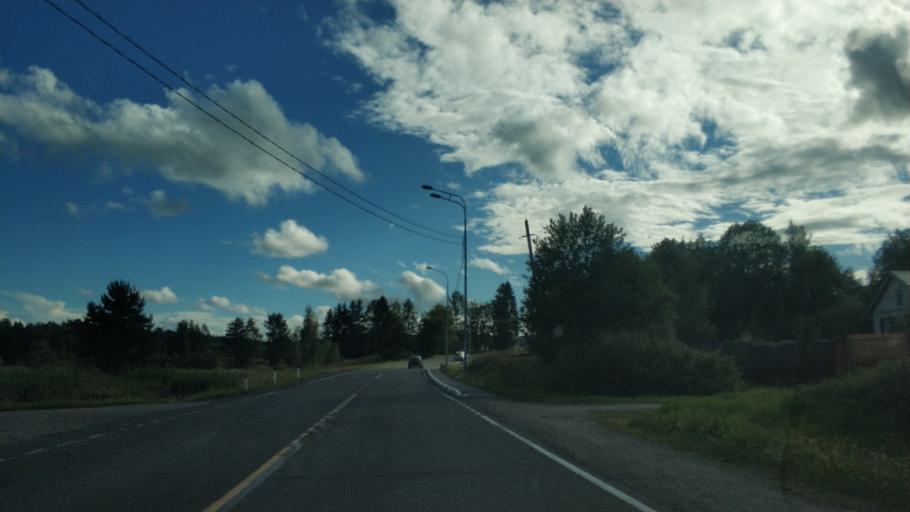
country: RU
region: Republic of Karelia
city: Lakhdenpokh'ya
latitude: 61.5541
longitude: 30.3219
